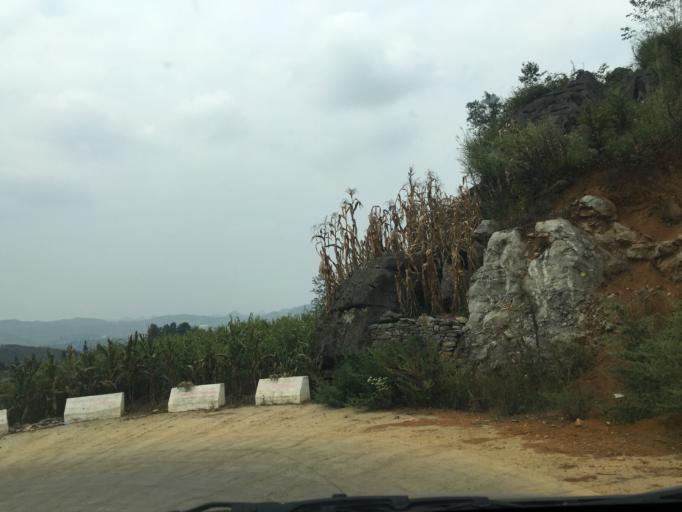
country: CN
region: Guangxi Zhuangzu Zizhiqu
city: Xinzhou
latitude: 25.5489
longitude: 105.5759
